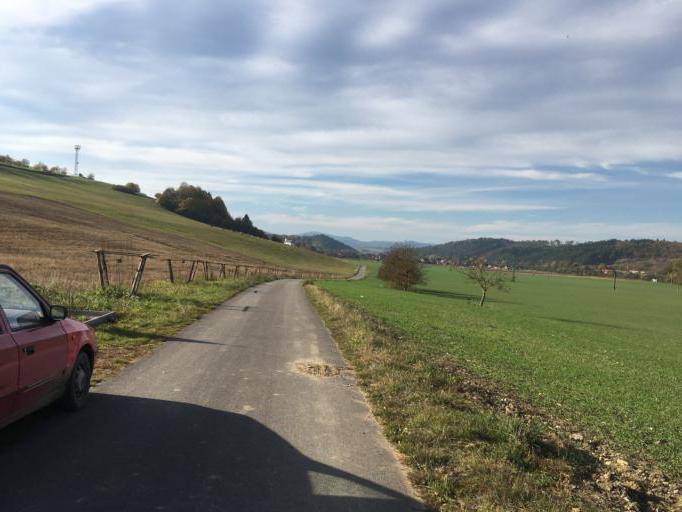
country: SK
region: Trenciansky
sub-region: Okres Povazska Bystrica
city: Povazska Bystrica
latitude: 49.0444
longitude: 18.4240
